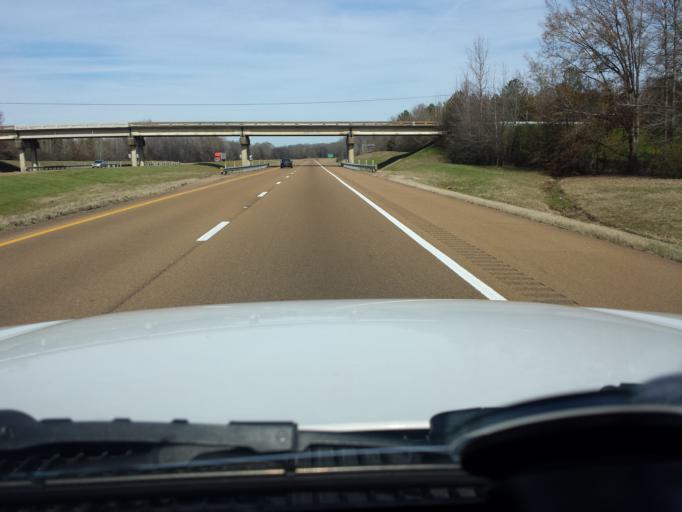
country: US
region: Mississippi
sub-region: Madison County
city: Canton
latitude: 32.6683
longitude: -90.0607
